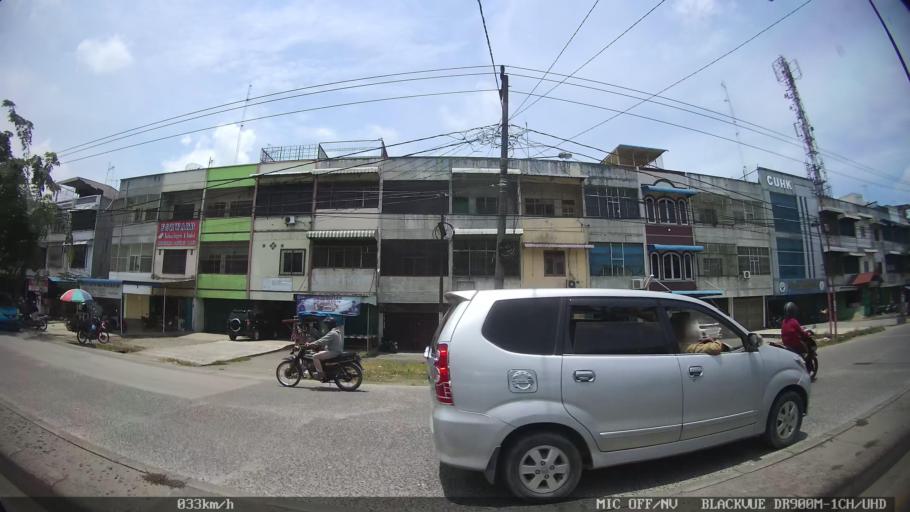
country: ID
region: North Sumatra
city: Labuhan Deli
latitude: 3.7216
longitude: 98.6798
